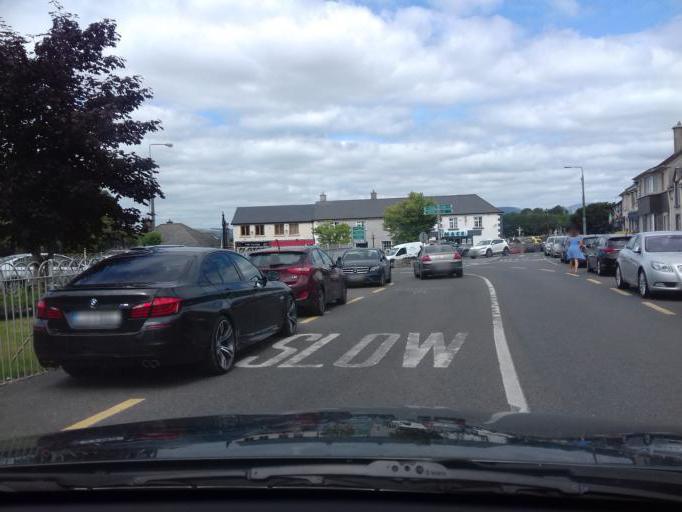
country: IE
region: Leinster
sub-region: Wicklow
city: Baltinglass
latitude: 52.8806
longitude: -6.6955
